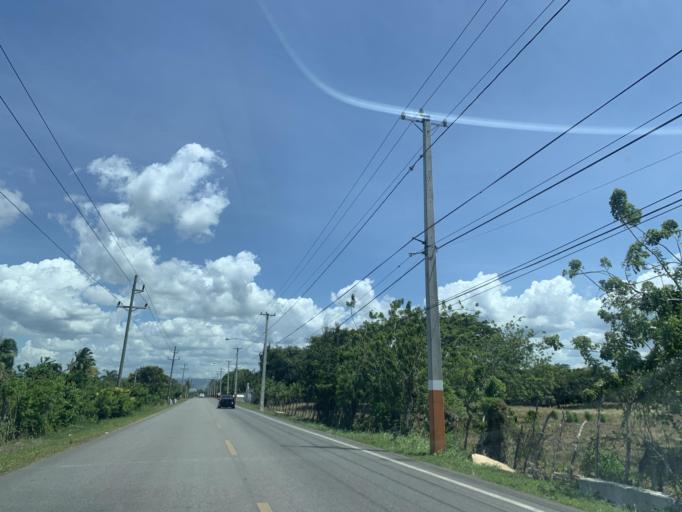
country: DO
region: Puerto Plata
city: Cabarete
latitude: 19.7191
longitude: -70.3864
